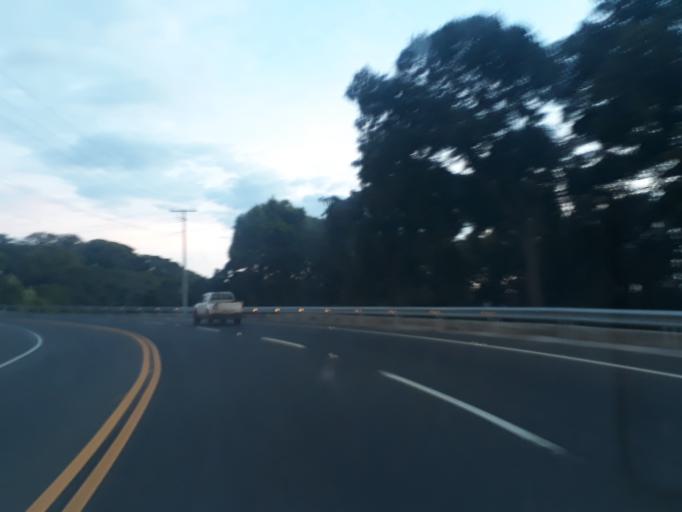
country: NI
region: Managua
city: El Crucero
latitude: 12.0294
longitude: -86.3129
